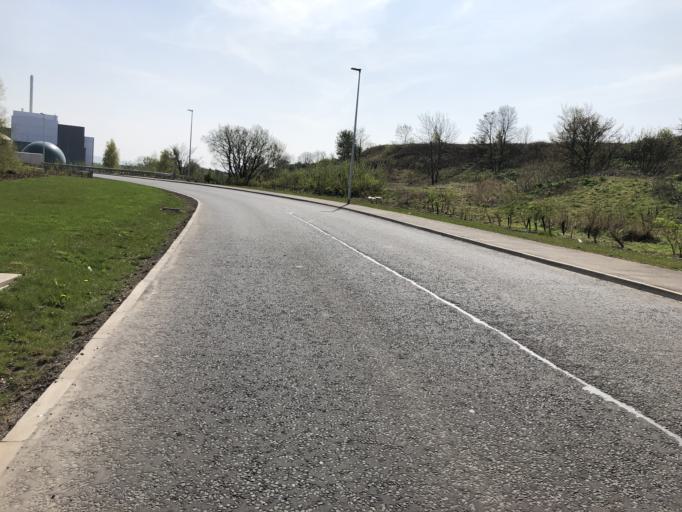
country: GB
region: Scotland
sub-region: Midlothian
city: Dalkeith
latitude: 55.9280
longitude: -3.0887
